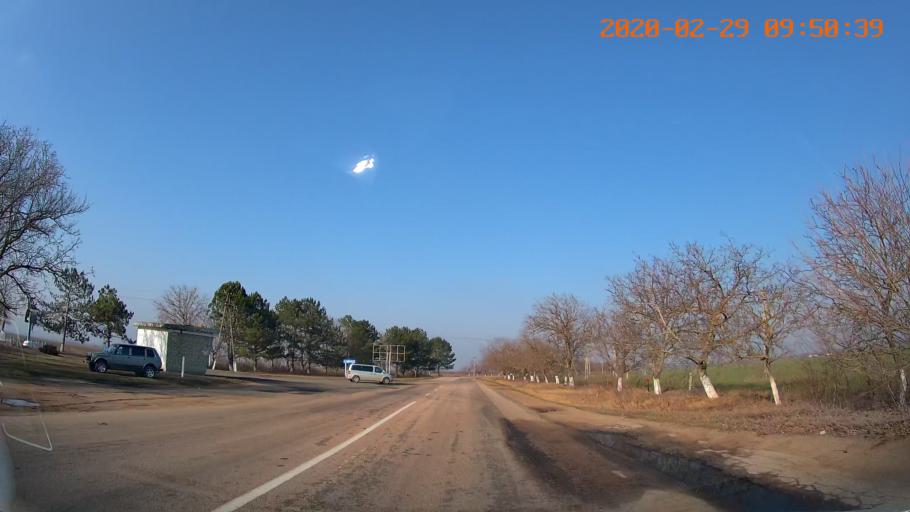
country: MD
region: Telenesti
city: Slobozia
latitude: 46.7029
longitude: 29.7521
